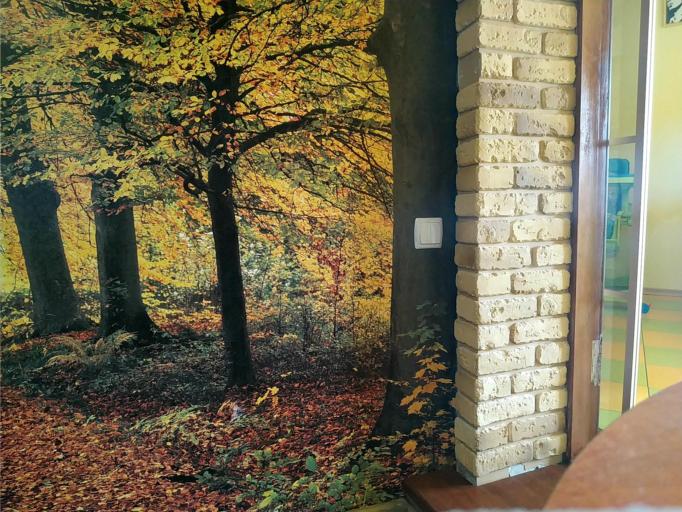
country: RU
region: Smolensk
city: Katyn'
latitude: 54.9442
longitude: 31.7188
